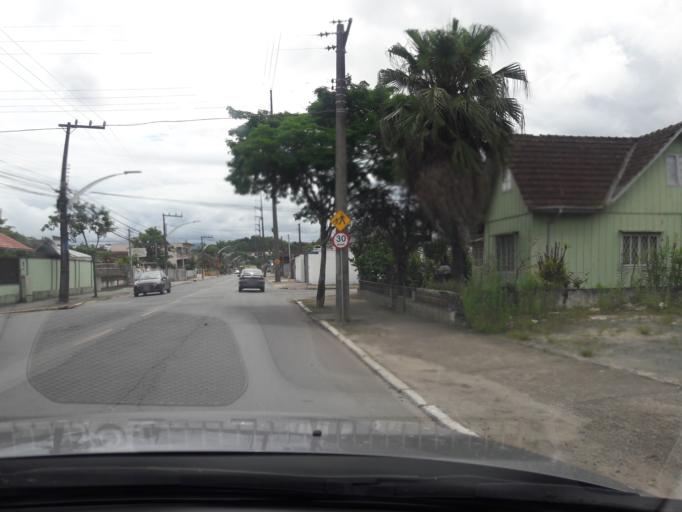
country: BR
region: Santa Catarina
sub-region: Joinville
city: Joinville
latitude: -26.3244
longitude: -48.8607
